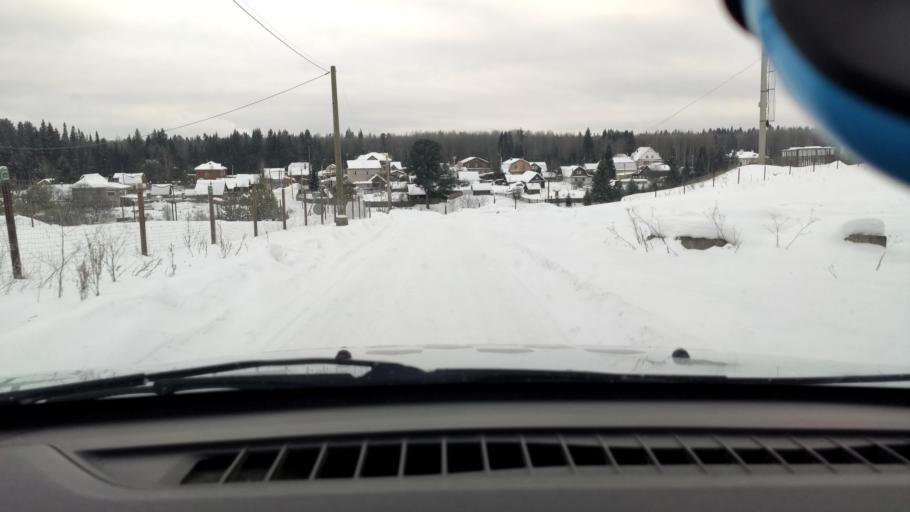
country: RU
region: Perm
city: Overyata
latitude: 58.0900
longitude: 55.9576
